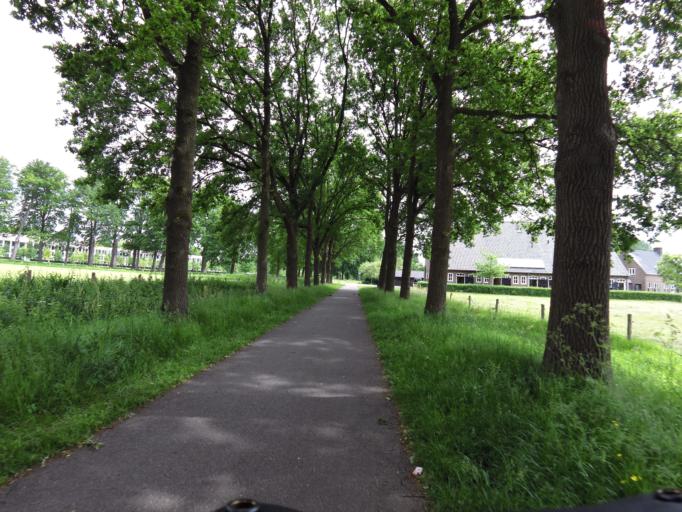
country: NL
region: North Brabant
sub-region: Gemeente Breda
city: Breda
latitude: 51.5592
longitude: 4.7848
